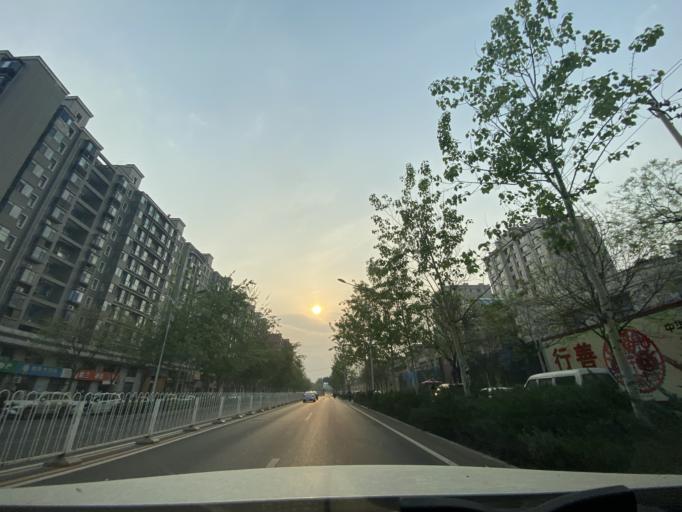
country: CN
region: Beijing
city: Babaoshan
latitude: 39.9284
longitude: 116.2369
